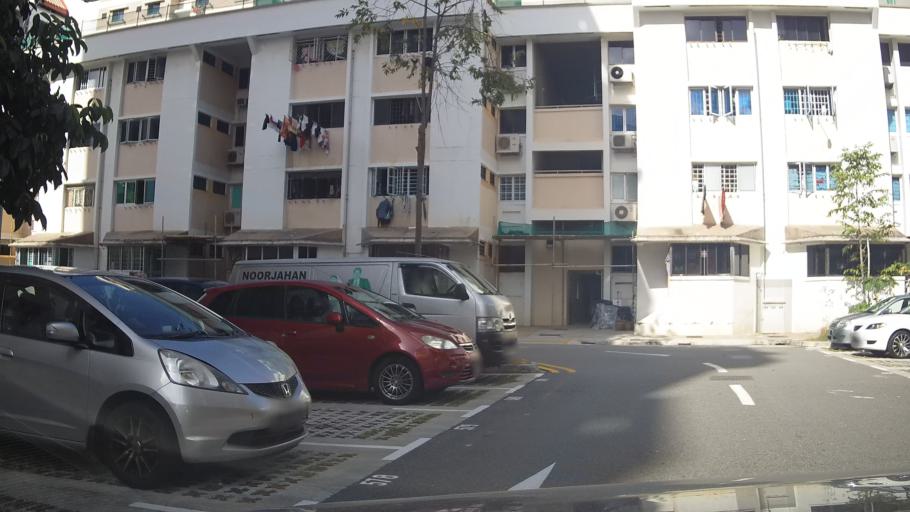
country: SG
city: Singapore
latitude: 1.3497
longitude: 103.9550
